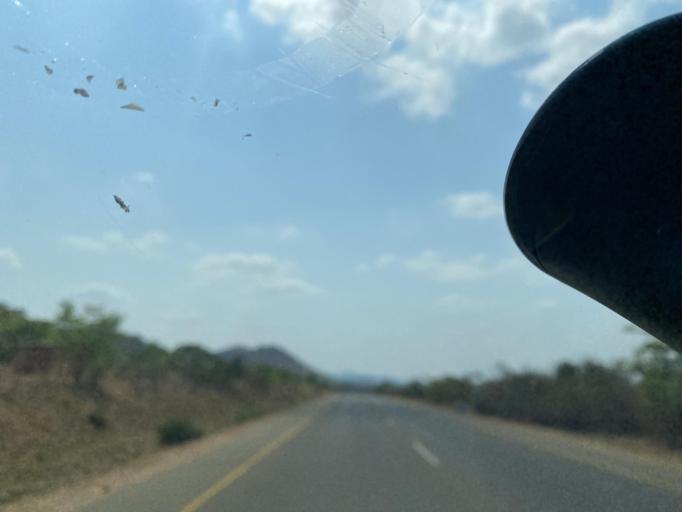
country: ZM
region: Lusaka
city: Chongwe
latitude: -15.5991
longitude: 28.7278
